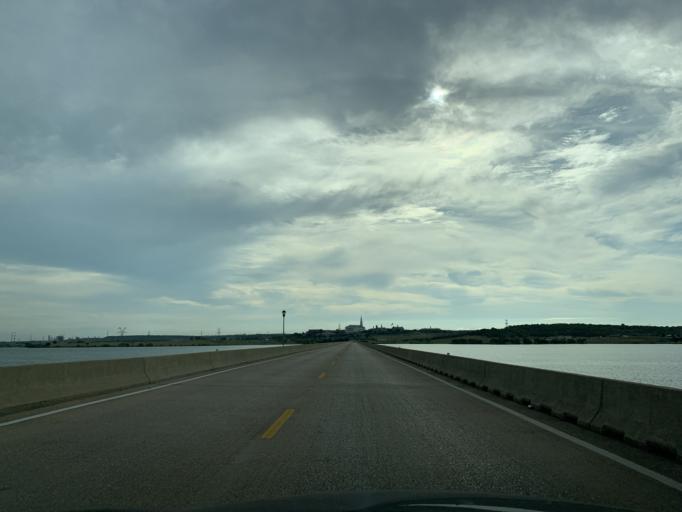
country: US
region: Texas
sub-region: Dallas County
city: Grand Prairie
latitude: 32.7070
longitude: -96.9662
